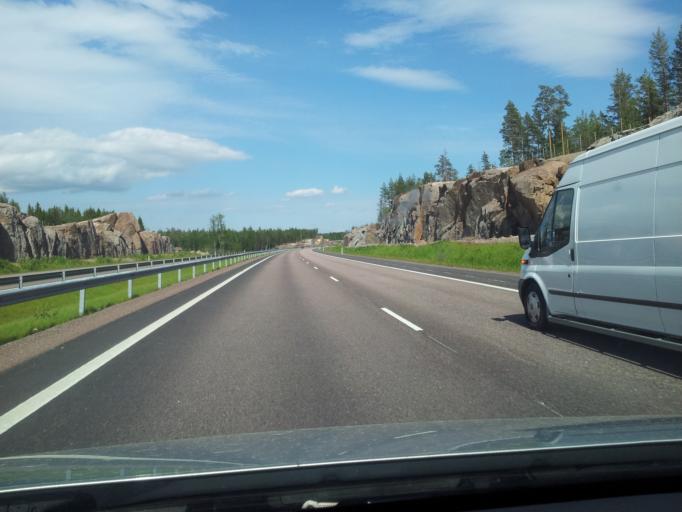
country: FI
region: Uusimaa
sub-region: Loviisa
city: Lovisa
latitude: 60.4820
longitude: 26.2849
